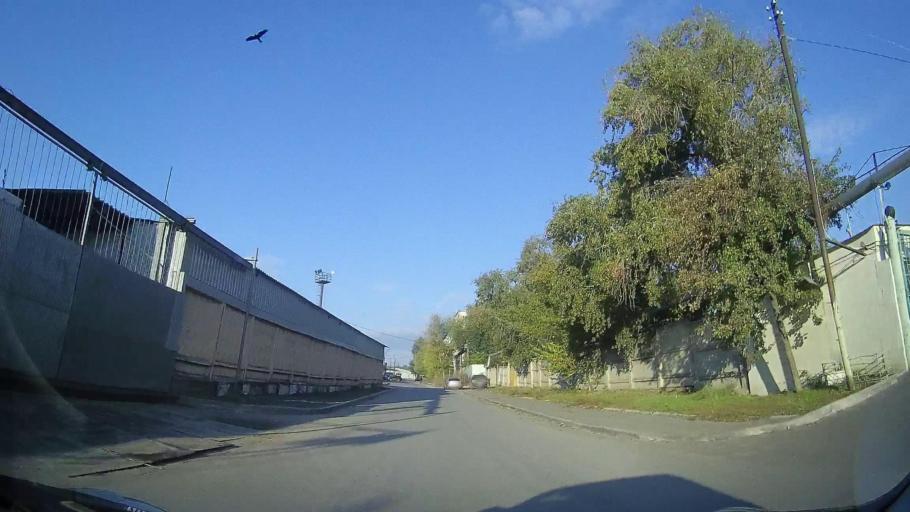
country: RU
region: Rostov
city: Severnyy
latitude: 47.2724
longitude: 39.6800
